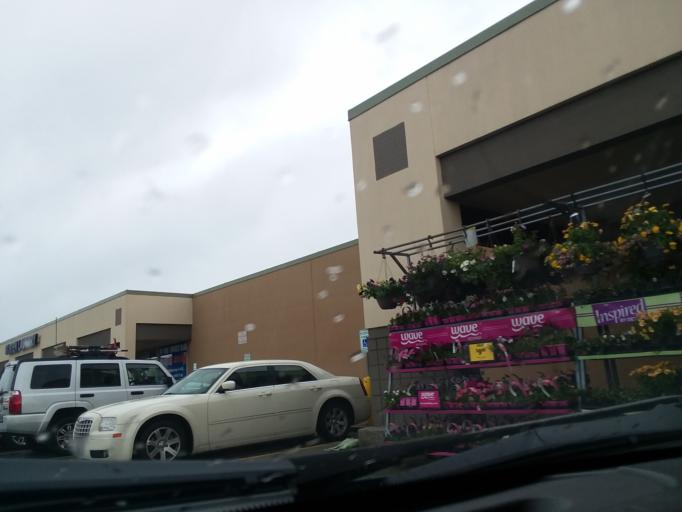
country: US
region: Washington
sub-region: King County
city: Burien
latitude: 47.4754
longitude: -122.3324
